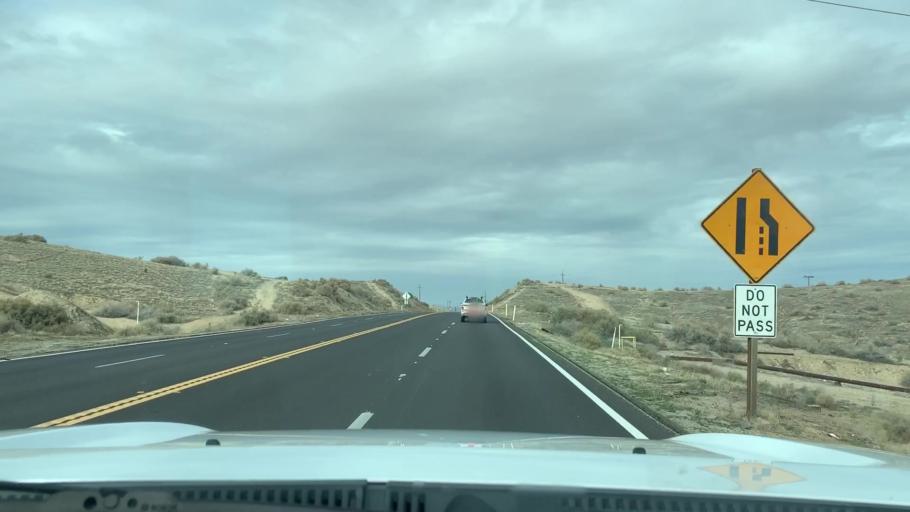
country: US
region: California
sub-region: Kern County
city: South Taft
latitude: 35.1189
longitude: -119.4332
